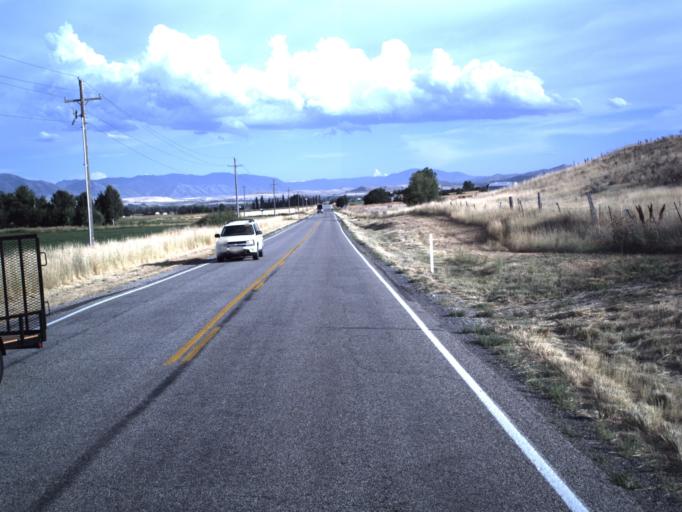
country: US
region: Utah
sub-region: Cache County
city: Mendon
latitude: 41.6971
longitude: -111.9743
